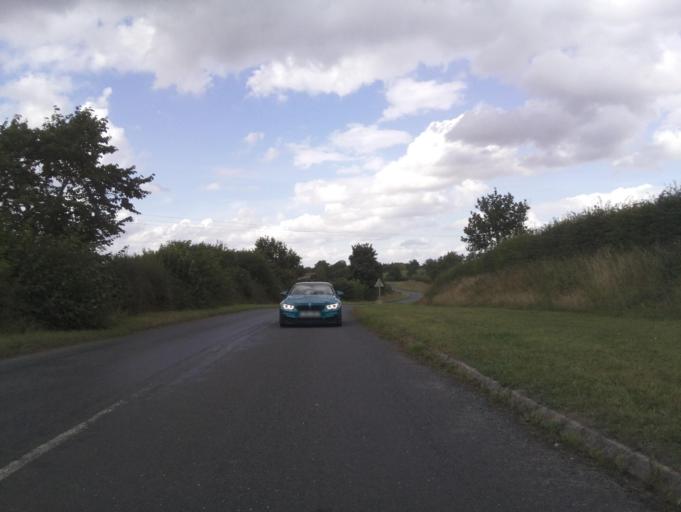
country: GB
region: England
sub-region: North Yorkshire
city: Bedale
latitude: 54.2476
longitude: -1.6940
